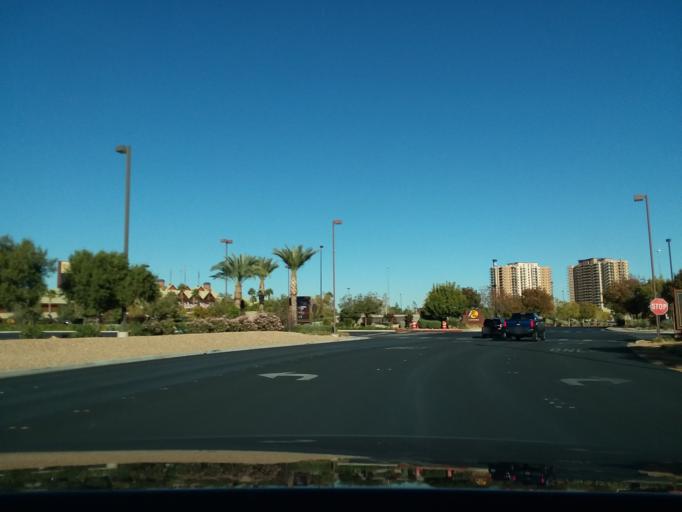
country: US
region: Nevada
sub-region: Clark County
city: Enterprise
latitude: 36.0389
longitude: -115.1842
